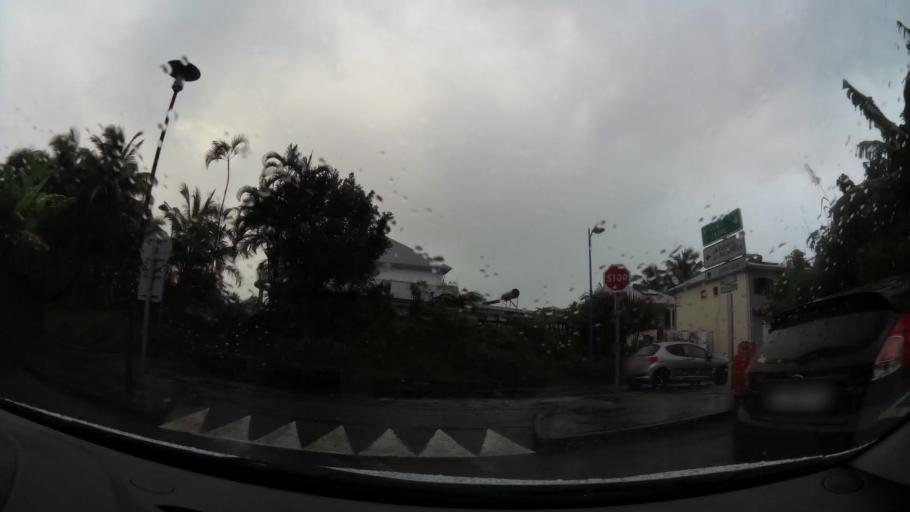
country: RE
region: Reunion
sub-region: Reunion
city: Saint-Benoit
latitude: -21.0403
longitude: 55.7155
